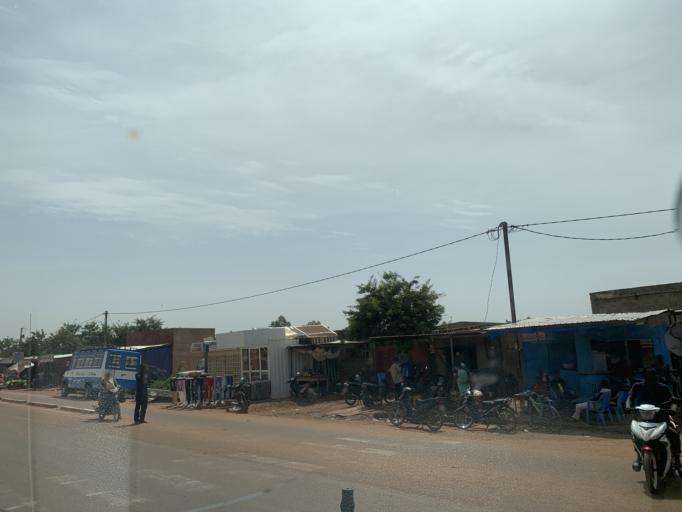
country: BF
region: Centre
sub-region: Kadiogo Province
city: Ouagadougou
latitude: 12.3345
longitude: -1.5200
